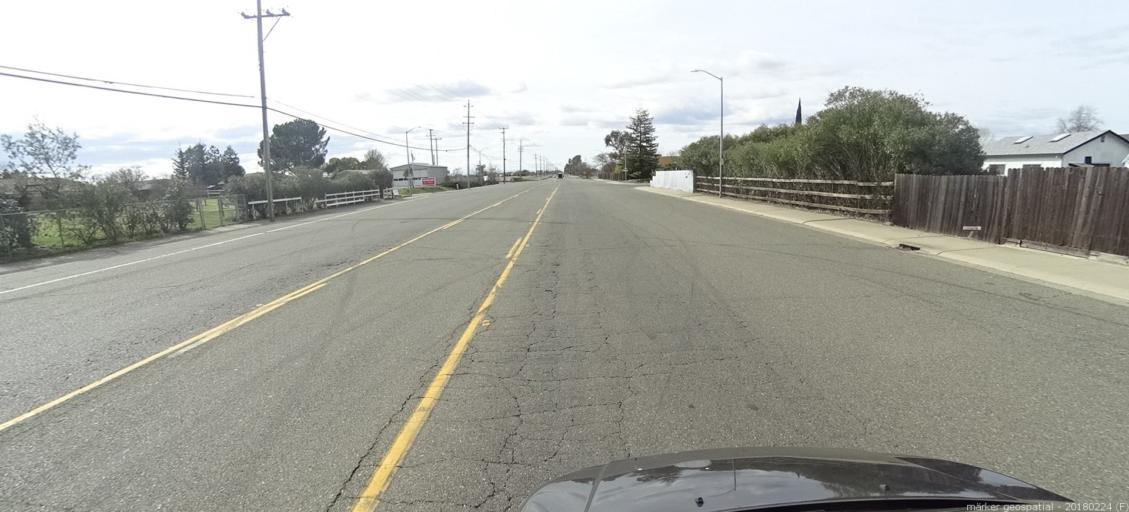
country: US
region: California
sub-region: Sacramento County
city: Rio Linda
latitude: 38.7144
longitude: -121.4179
